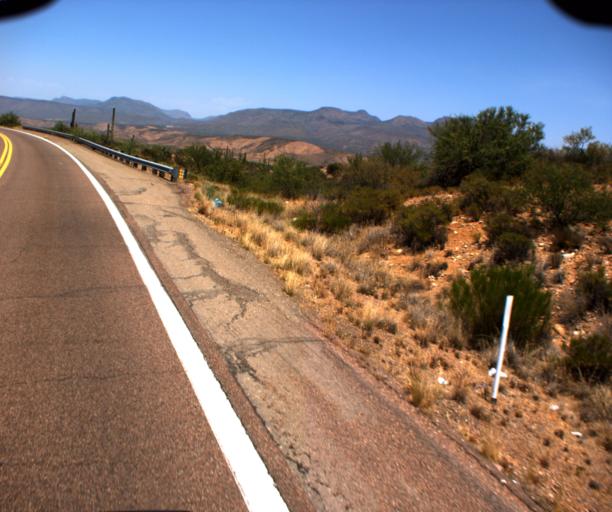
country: US
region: Arizona
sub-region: Gila County
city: Tonto Basin
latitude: 33.7313
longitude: -111.2116
